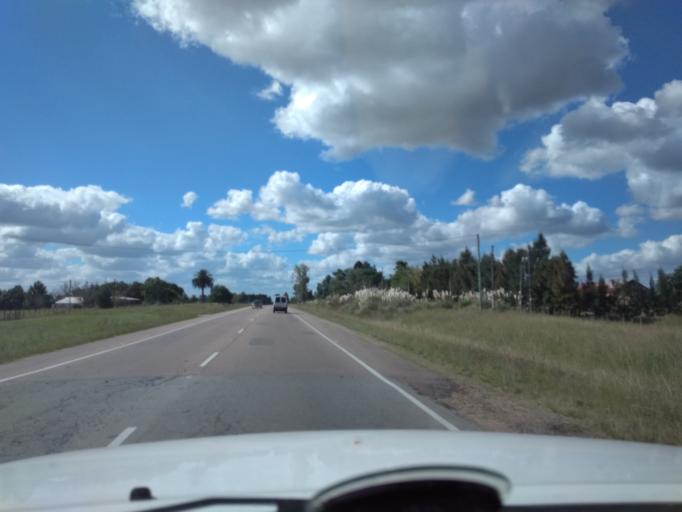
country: UY
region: Canelones
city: Sauce
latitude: -34.6807
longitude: -56.0522
